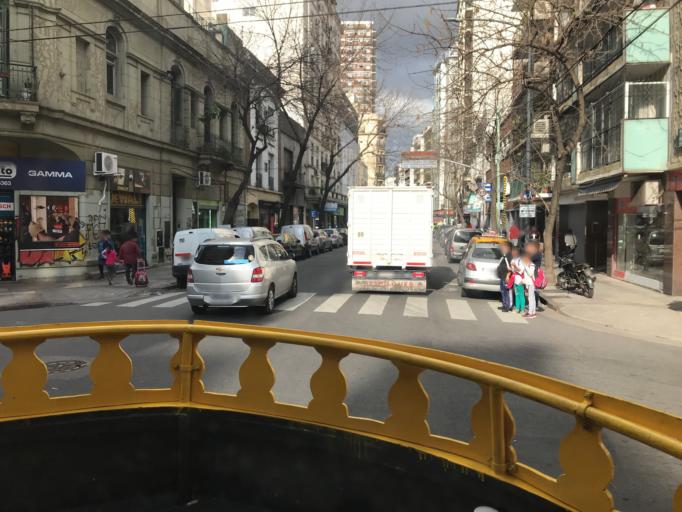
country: AR
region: Buenos Aires F.D.
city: Buenos Aires
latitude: -34.6054
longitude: -58.4070
